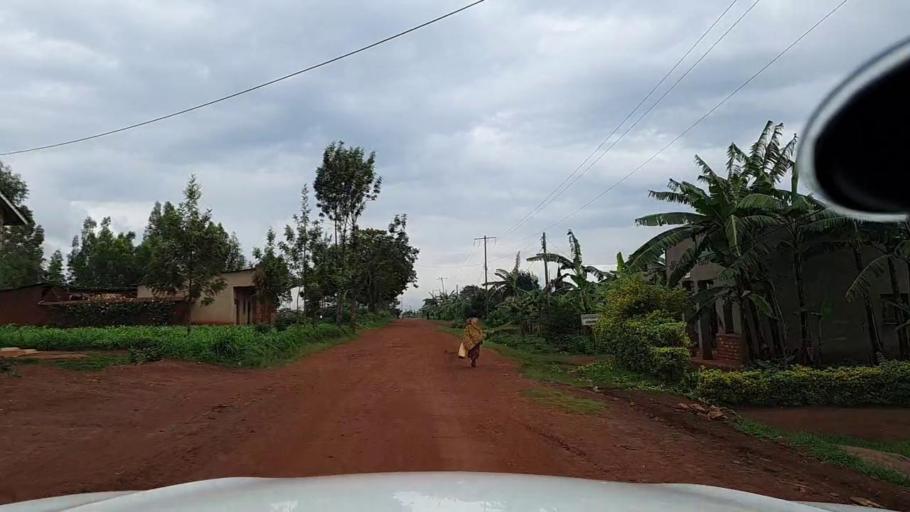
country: RW
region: Kigali
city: Kigali
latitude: -1.9293
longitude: 29.9002
